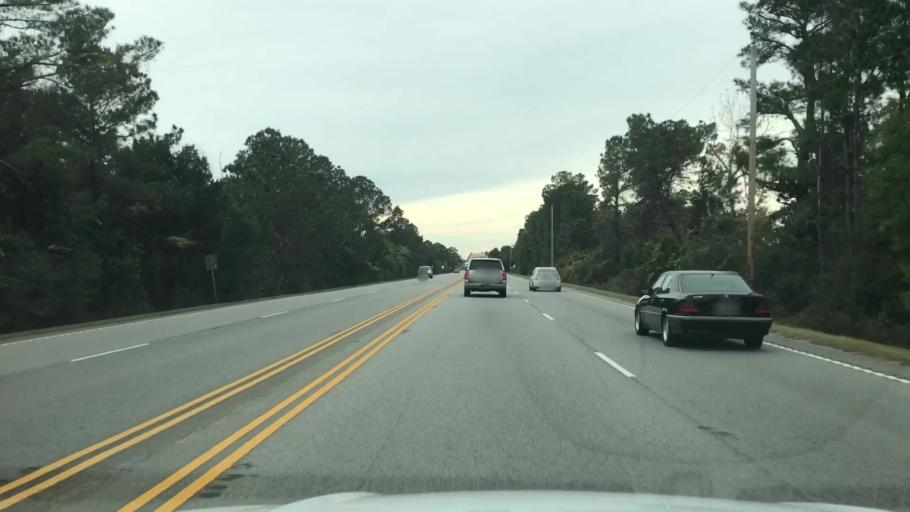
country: US
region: South Carolina
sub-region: Georgetown County
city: Georgetown
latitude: 33.3647
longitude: -79.2424
